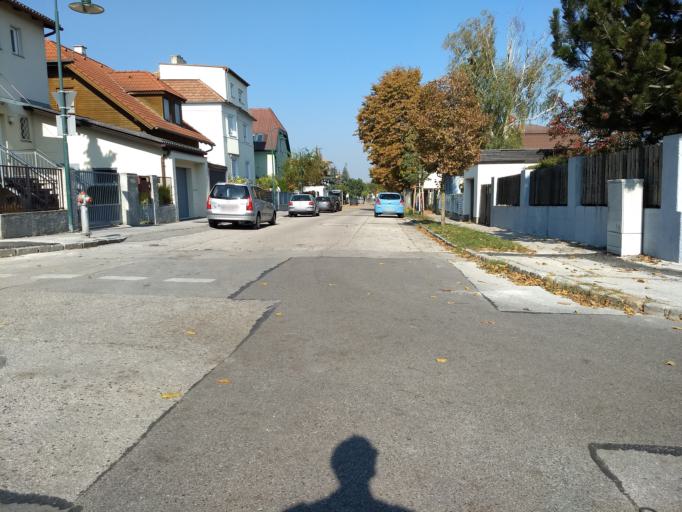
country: AT
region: Lower Austria
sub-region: Politischer Bezirk Modling
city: Brunn am Gebirge
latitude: 48.1113
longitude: 16.2807
